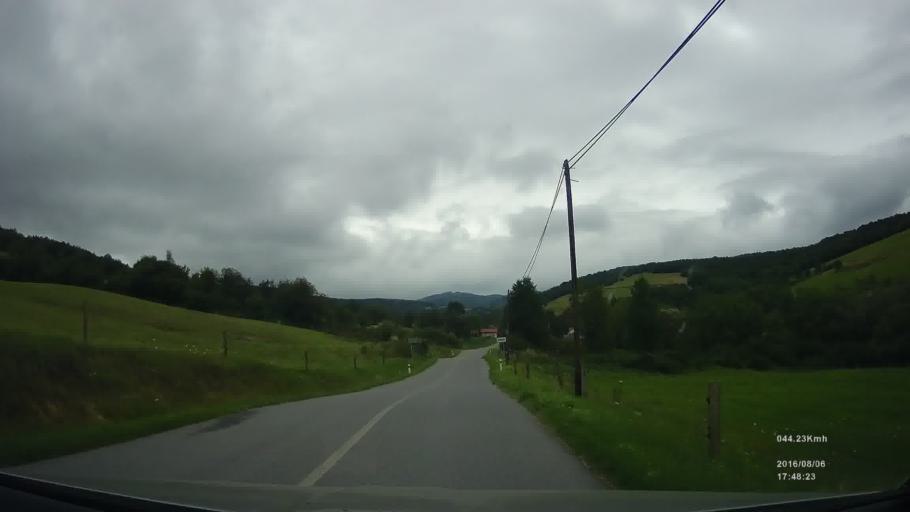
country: SK
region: Presovsky
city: Svidnik
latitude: 49.3764
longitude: 21.5733
